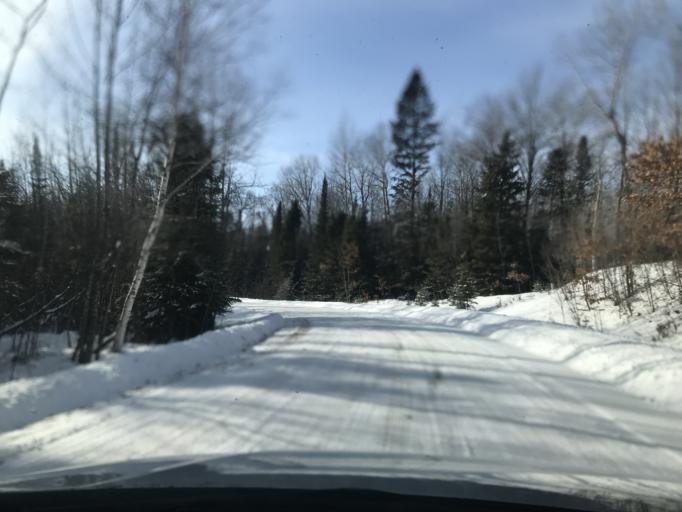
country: US
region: Wisconsin
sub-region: Oconto County
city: Gillett
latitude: 45.1485
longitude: -88.2269
